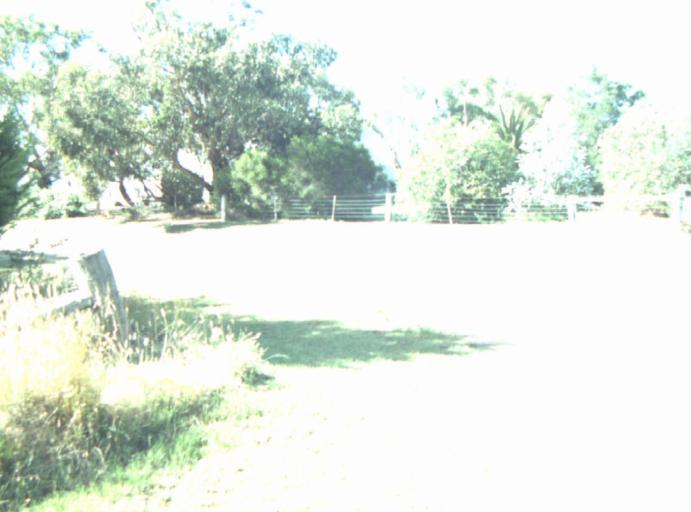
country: AU
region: Victoria
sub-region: Greater Geelong
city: Clifton Springs
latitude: -38.2221
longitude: 144.5892
